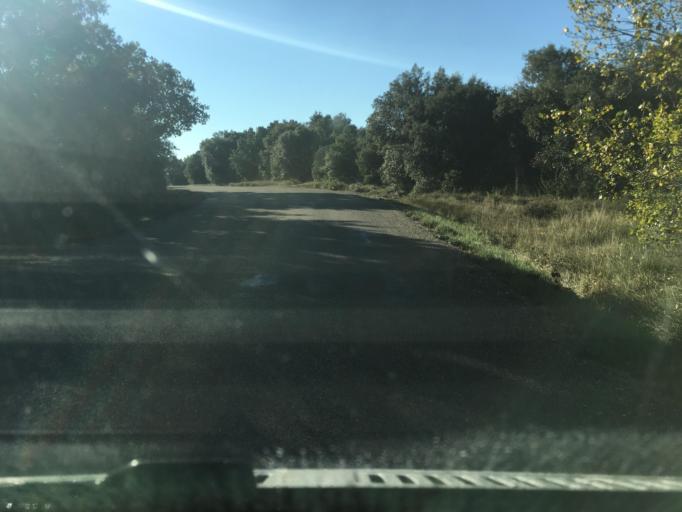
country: FR
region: Languedoc-Roussillon
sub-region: Departement du Gard
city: Goudargues
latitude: 44.1700
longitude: 4.3472
